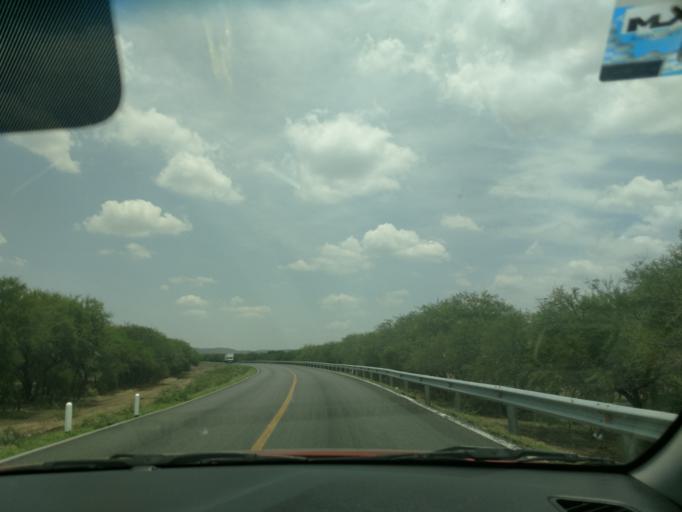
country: MX
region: San Luis Potosi
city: Zaragoza
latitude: 22.0188
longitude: -100.3991
